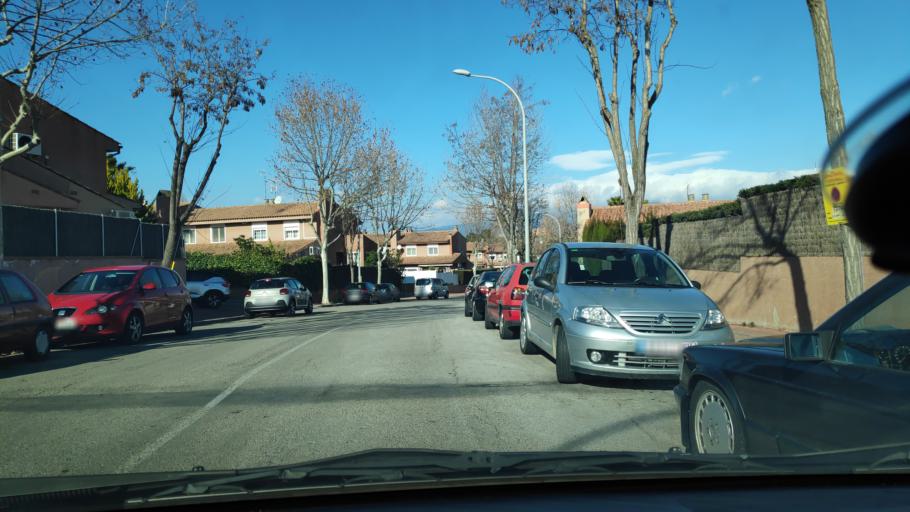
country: ES
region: Catalonia
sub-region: Provincia de Barcelona
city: Sant Quirze del Valles
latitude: 41.5287
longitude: 2.0746
